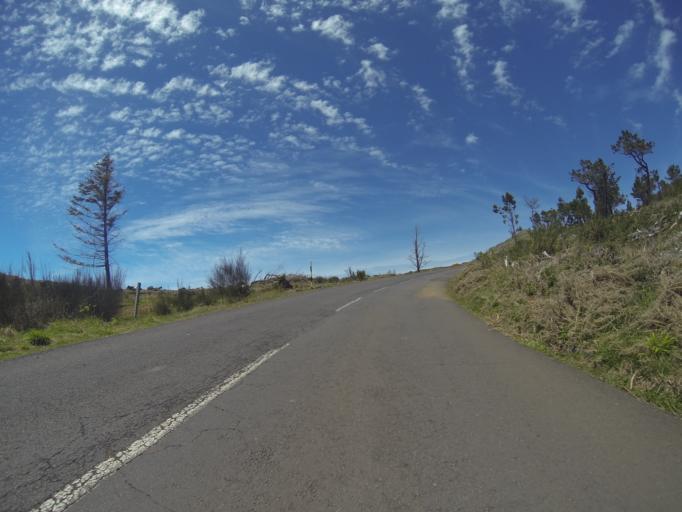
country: PT
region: Madeira
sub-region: Funchal
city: Nossa Senhora do Monte
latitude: 32.7159
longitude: -16.9021
